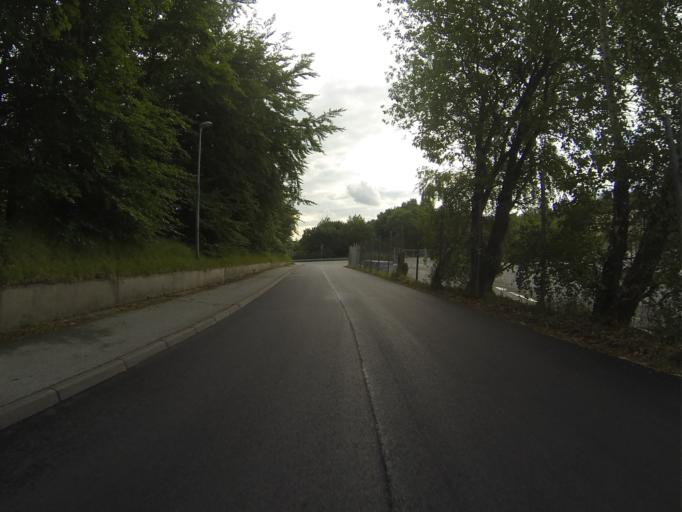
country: SE
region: Skane
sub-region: Lunds Kommun
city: Genarp
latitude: 55.6942
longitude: 13.3521
